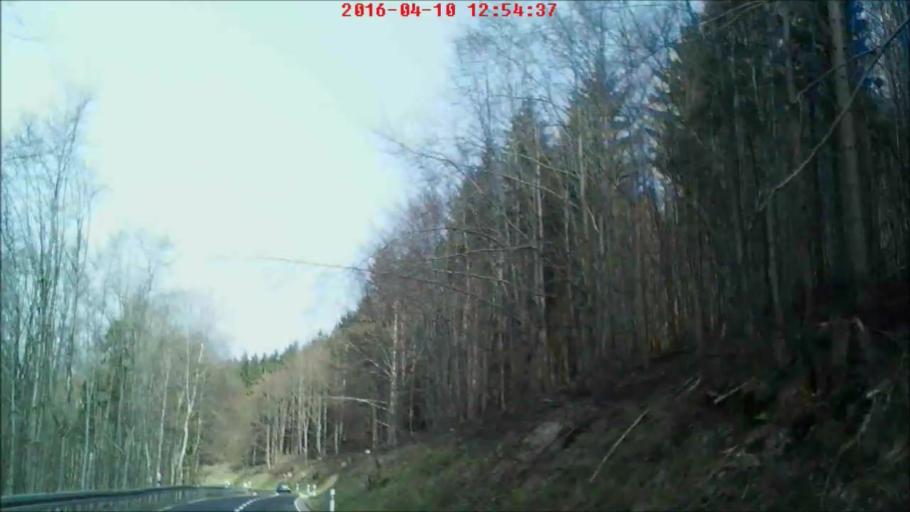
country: DE
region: Thuringia
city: Pappenheim
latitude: 50.8192
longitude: 10.5191
